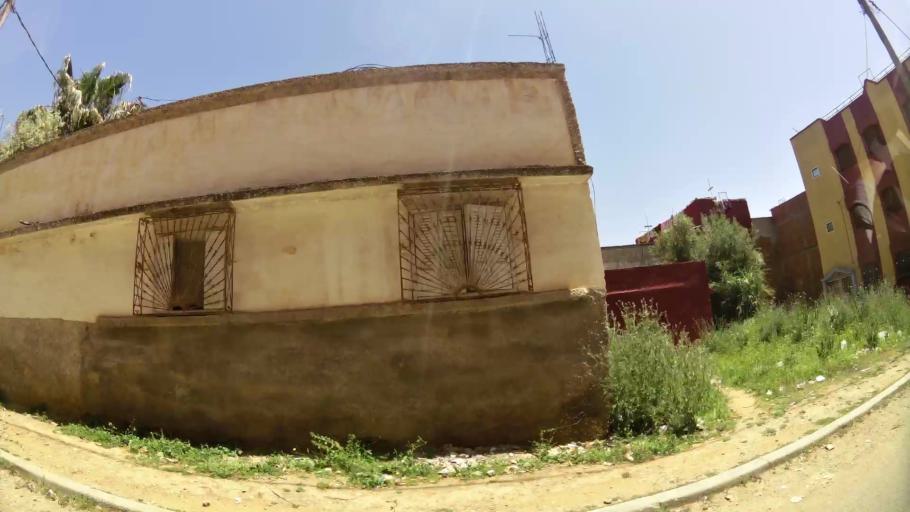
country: MA
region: Rabat-Sale-Zemmour-Zaer
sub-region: Khemisset
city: Khemisset
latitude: 33.8334
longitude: -6.0696
